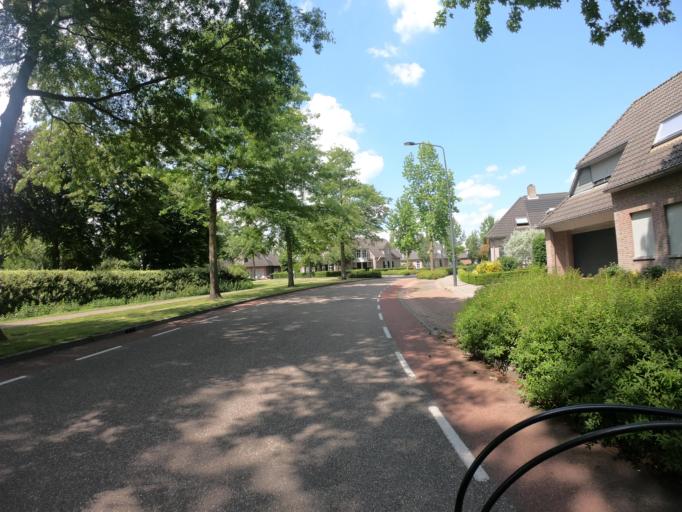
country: NL
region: North Brabant
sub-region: Gemeente Uden
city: Uden
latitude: 51.6426
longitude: 5.6225
